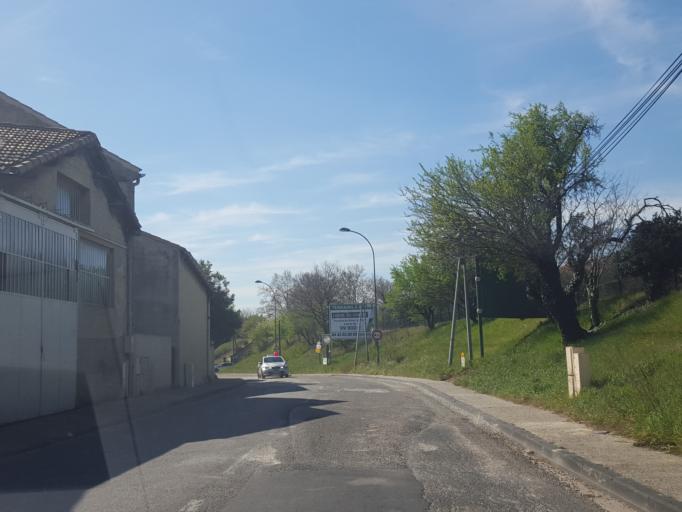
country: FR
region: Provence-Alpes-Cote d'Azur
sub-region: Departement du Vaucluse
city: Carpentras
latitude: 44.0449
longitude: 5.0462
